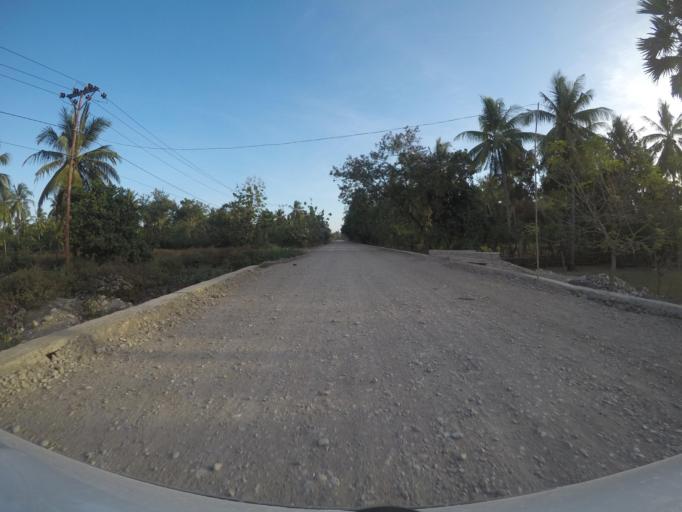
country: TL
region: Viqueque
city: Viqueque
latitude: -8.8545
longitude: 126.5113
